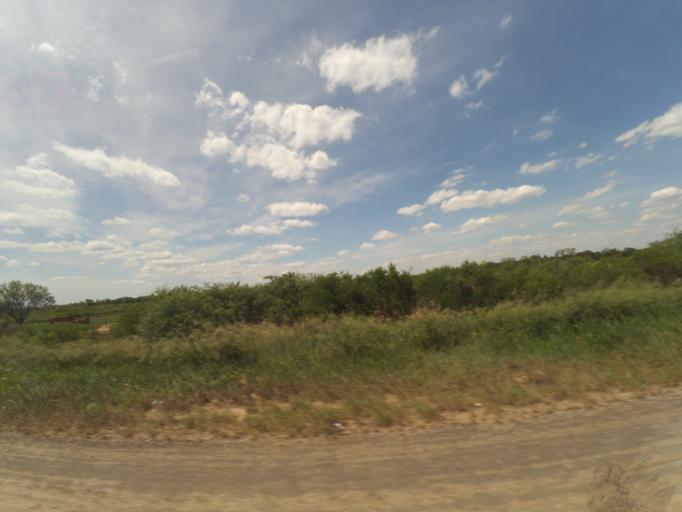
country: BO
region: Santa Cruz
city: Pailon
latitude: -17.5888
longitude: -61.9615
